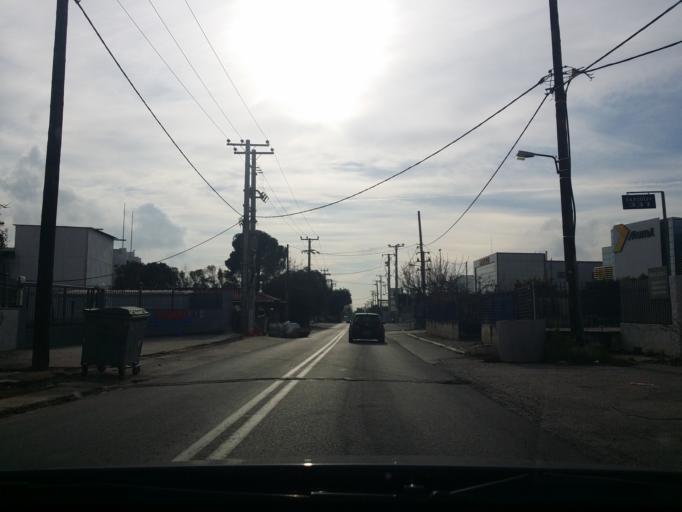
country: GR
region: Attica
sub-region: Nomarchia Athinas
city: Metamorfosi
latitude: 38.0857
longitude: 23.7685
